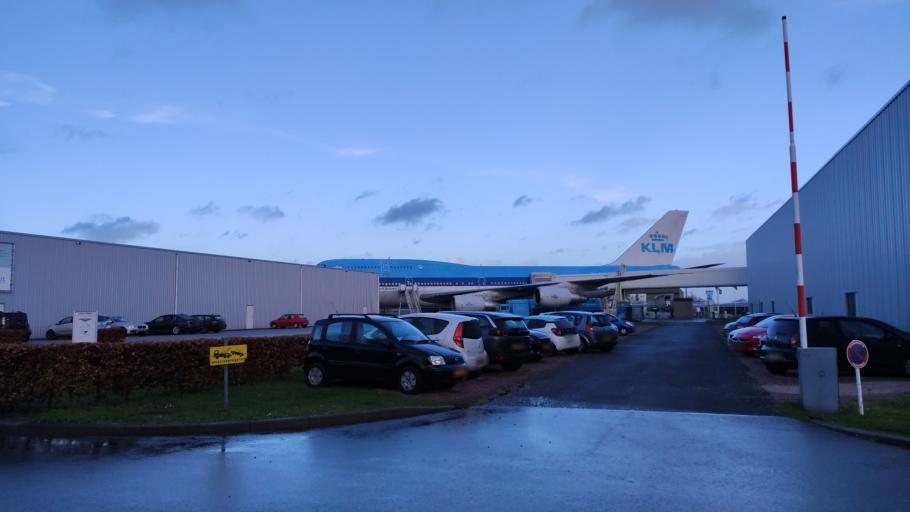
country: NL
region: Flevoland
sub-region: Gemeente Lelystad
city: Lelystad
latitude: 52.4573
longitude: 5.5283
